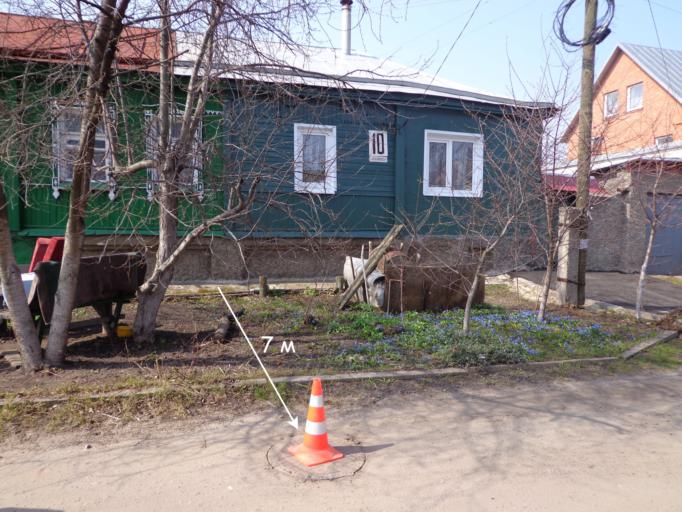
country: RU
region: Voronezj
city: Voronezh
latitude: 51.7060
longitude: 39.2347
